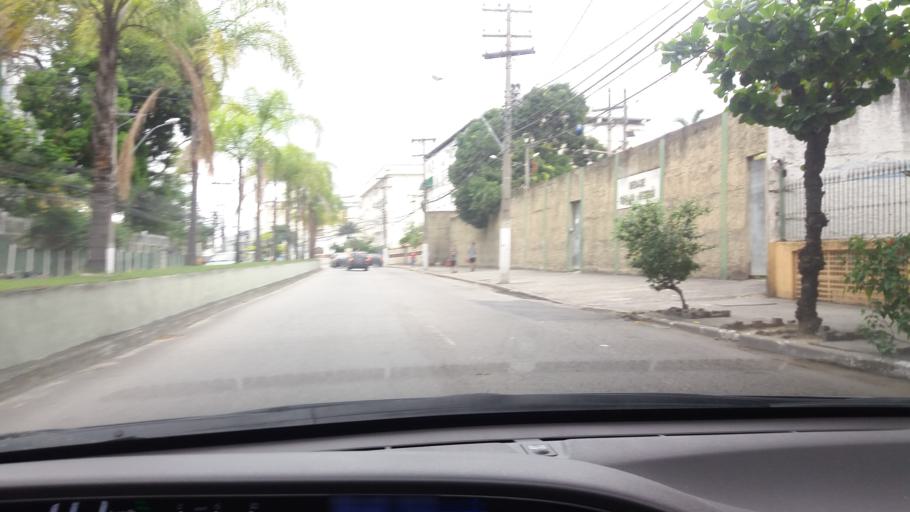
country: BR
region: Rio de Janeiro
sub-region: Niteroi
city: Niteroi
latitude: -22.8734
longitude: -43.1059
